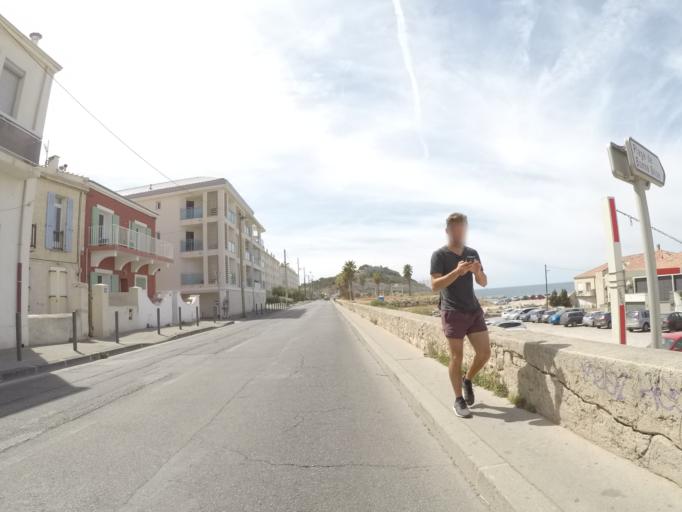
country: FR
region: Provence-Alpes-Cote d'Azur
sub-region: Departement des Bouches-du-Rhone
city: Marseille 08
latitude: 43.2354
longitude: 5.3608
